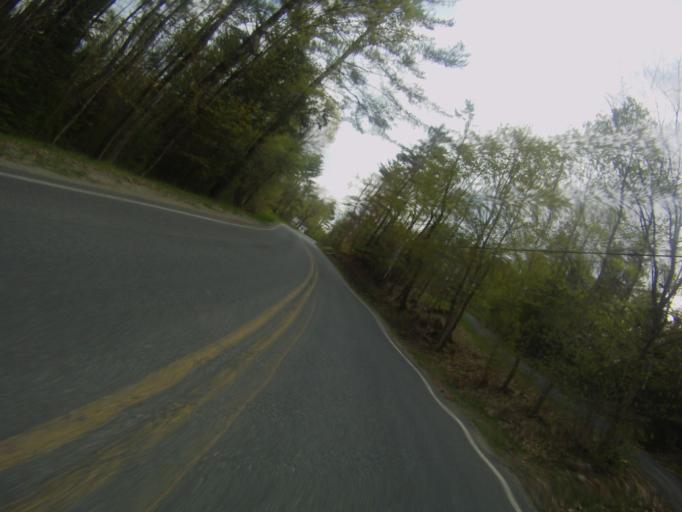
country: US
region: New York
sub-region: Warren County
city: Warrensburg
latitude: 43.8424
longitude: -73.8720
